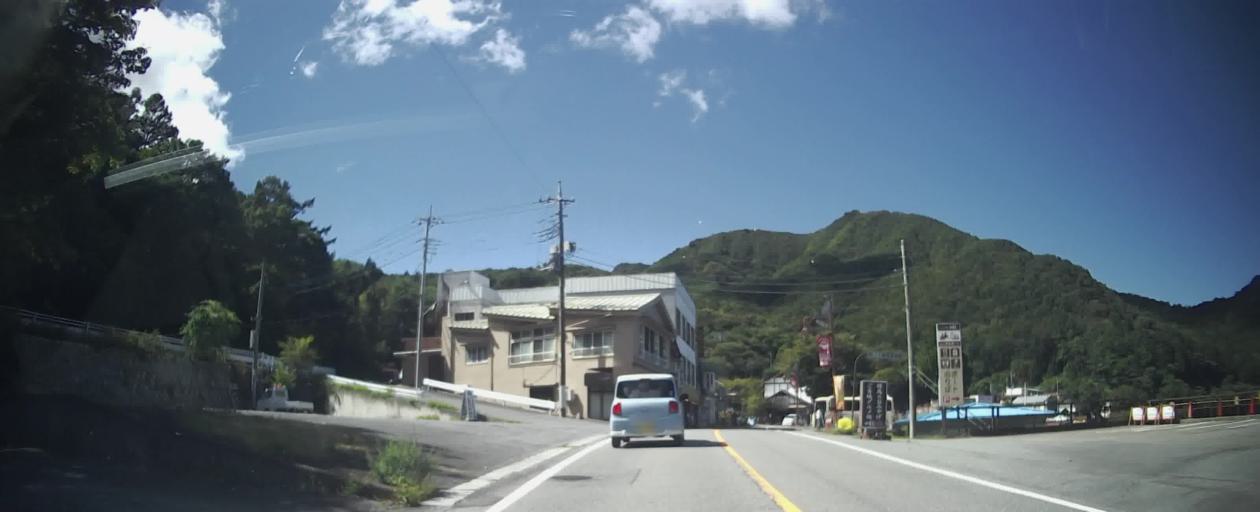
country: JP
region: Gunma
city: Nakanojomachi
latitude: 36.4698
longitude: 138.8616
